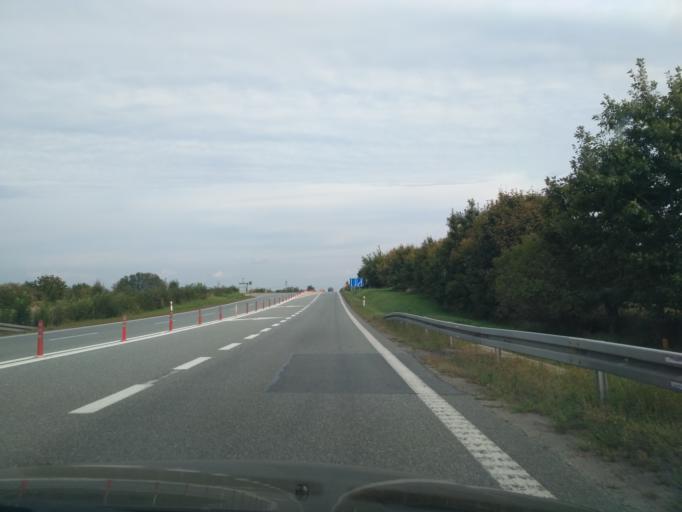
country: PL
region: Subcarpathian Voivodeship
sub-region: Powiat rzeszowski
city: Trzciana
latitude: 50.0715
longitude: 21.8646
